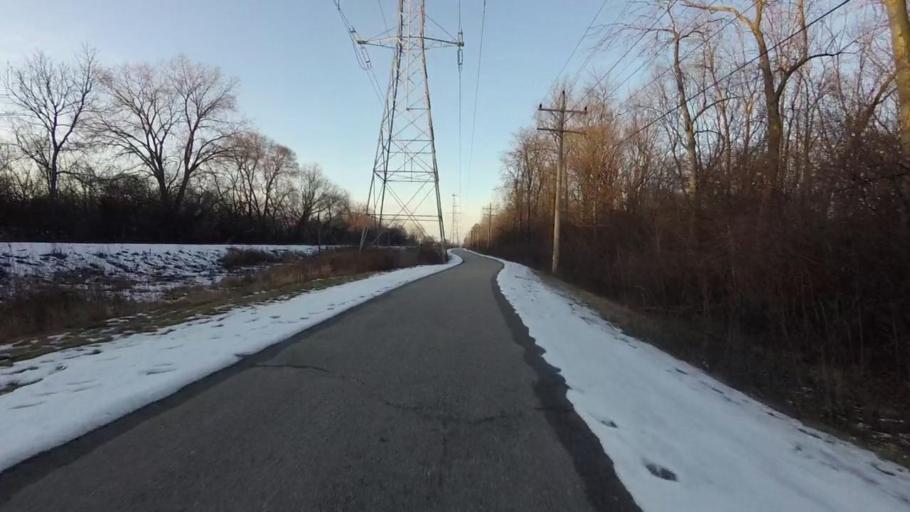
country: US
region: Wisconsin
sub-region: Milwaukee County
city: Brown Deer
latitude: 43.1589
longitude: -87.9590
